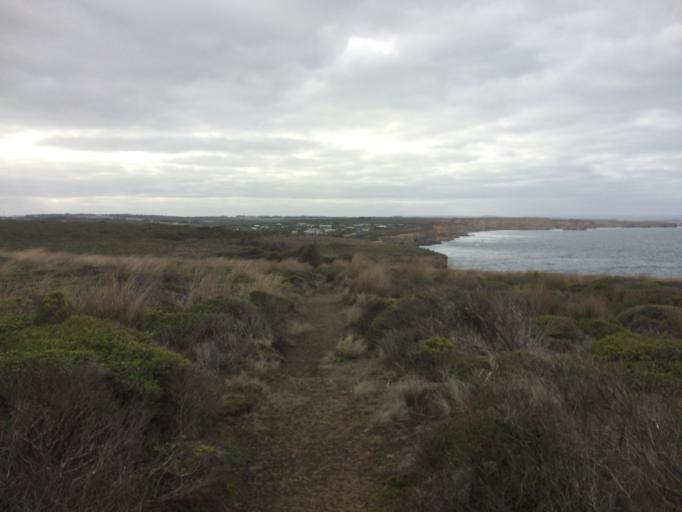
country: AU
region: Victoria
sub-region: Warrnambool
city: Allansford
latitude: -38.6236
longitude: 142.9805
